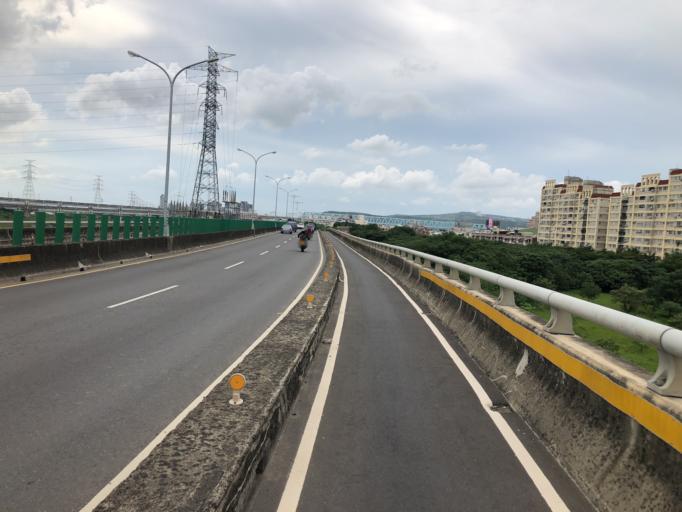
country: TW
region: Taiwan
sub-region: Changhua
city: Chang-hua
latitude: 24.0999
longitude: 120.6248
